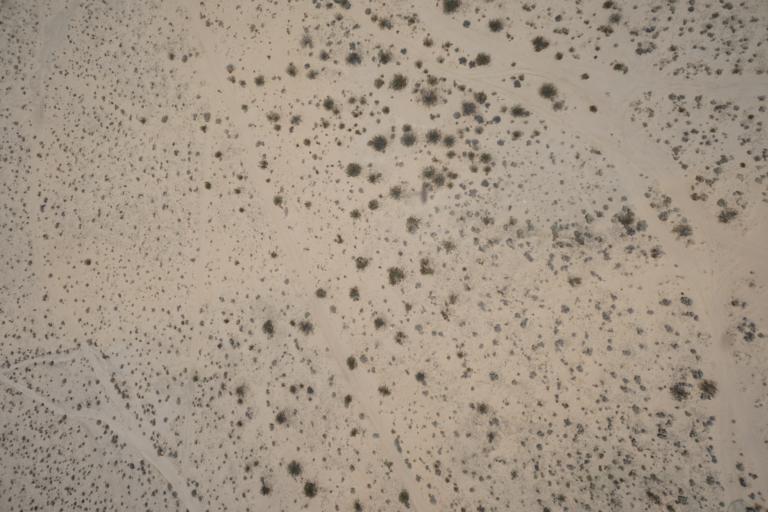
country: US
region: California
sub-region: San Bernardino County
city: Twentynine Palms
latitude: 34.1604
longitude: -116.0449
